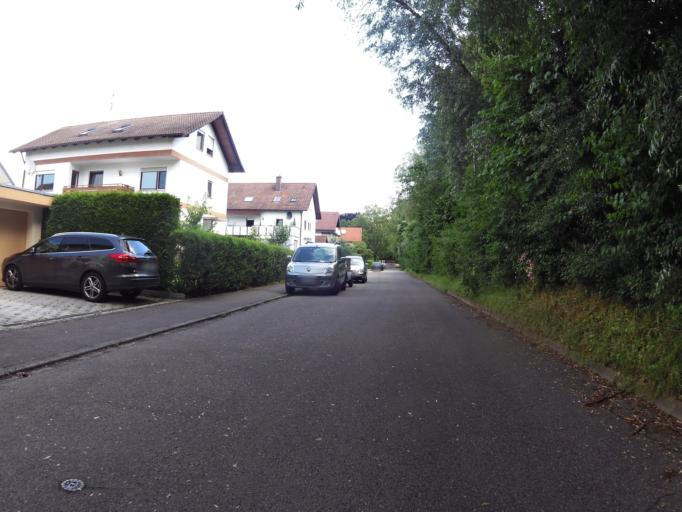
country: DE
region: Baden-Wuerttemberg
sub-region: Freiburg Region
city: Kippenheim
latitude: 48.3300
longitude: 7.8221
